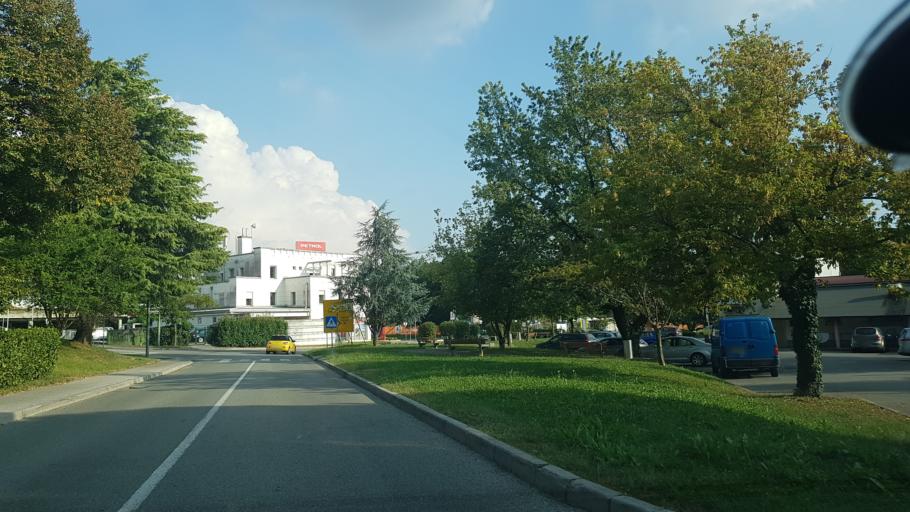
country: IT
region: Friuli Venezia Giulia
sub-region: Provincia di Gorizia
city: Gorizia
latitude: 45.9427
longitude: 13.6369
